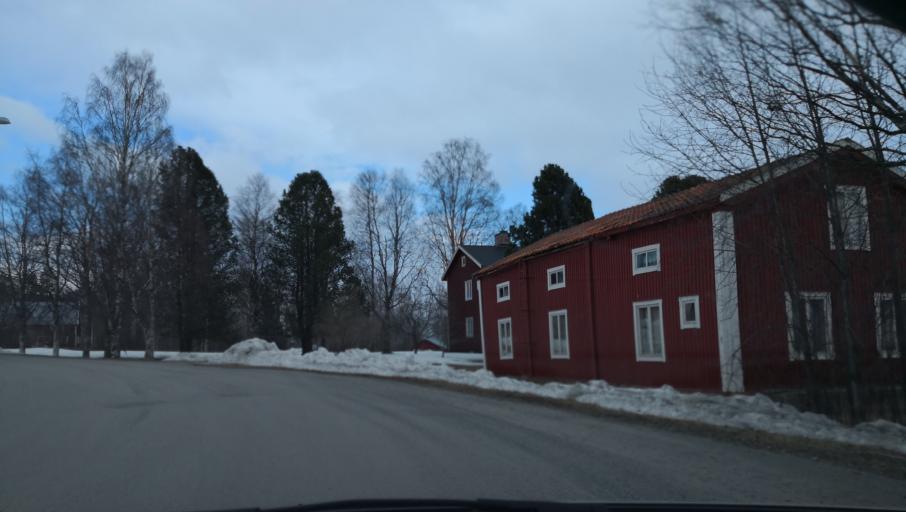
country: SE
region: Vaesterbotten
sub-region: Vannas Kommun
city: Vannasby
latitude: 63.9156
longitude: 19.8146
